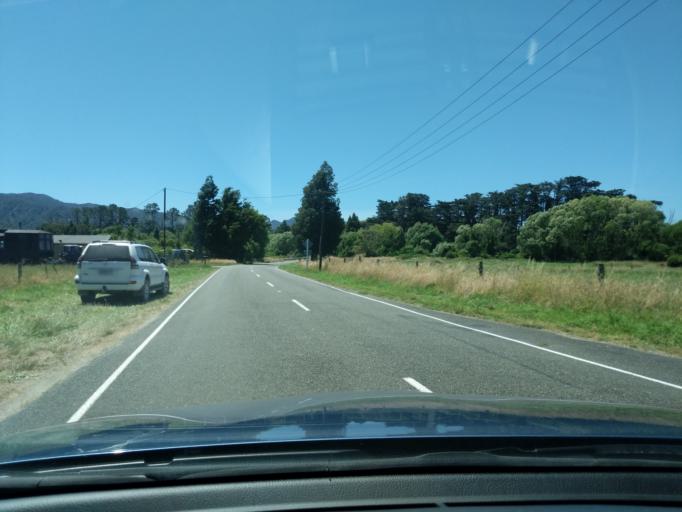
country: NZ
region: Tasman
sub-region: Tasman District
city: Takaka
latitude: -40.7651
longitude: 172.5634
